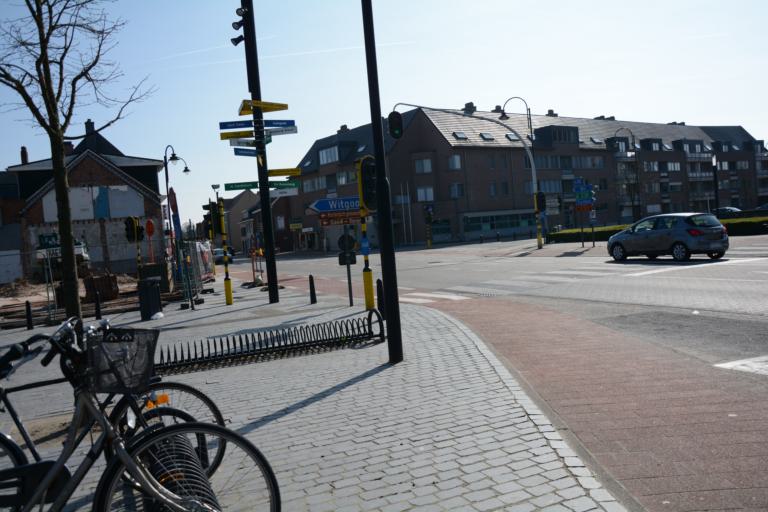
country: BE
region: Flanders
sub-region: Provincie Antwerpen
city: Dessel
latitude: 51.2396
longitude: 5.1131
